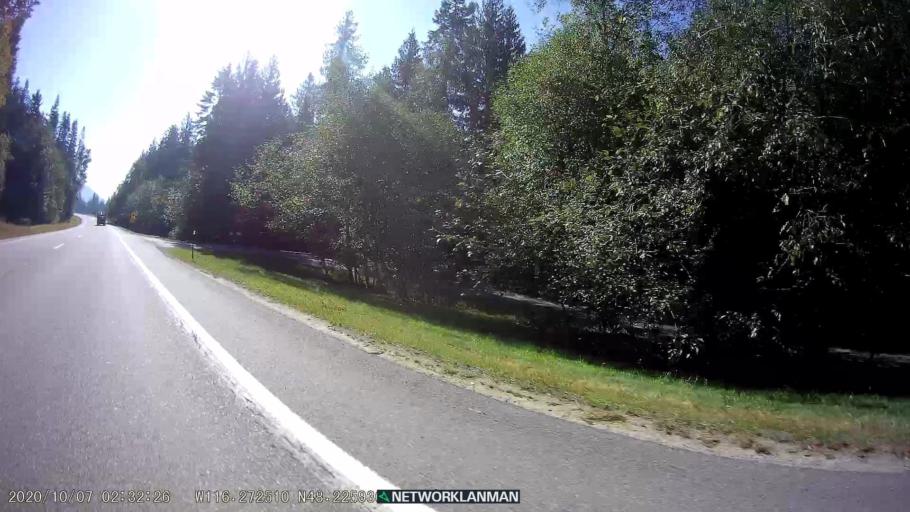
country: US
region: Idaho
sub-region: Bonner County
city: Ponderay
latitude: 48.2254
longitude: -116.2722
